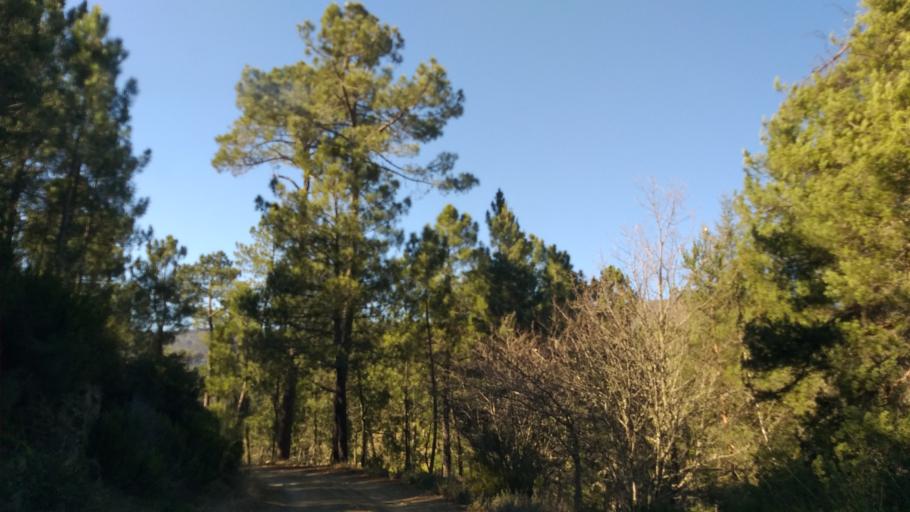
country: PT
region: Guarda
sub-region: Manteigas
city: Manteigas
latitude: 40.4430
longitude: -7.5095
